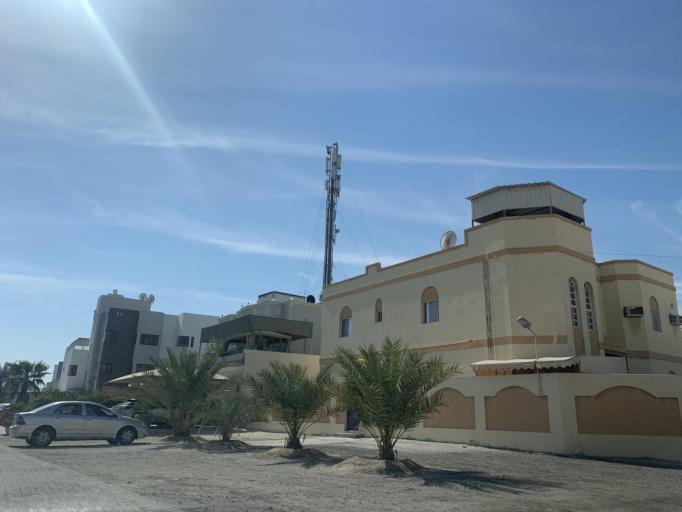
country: BH
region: Central Governorate
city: Madinat Hamad
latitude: 26.1179
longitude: 50.4849
